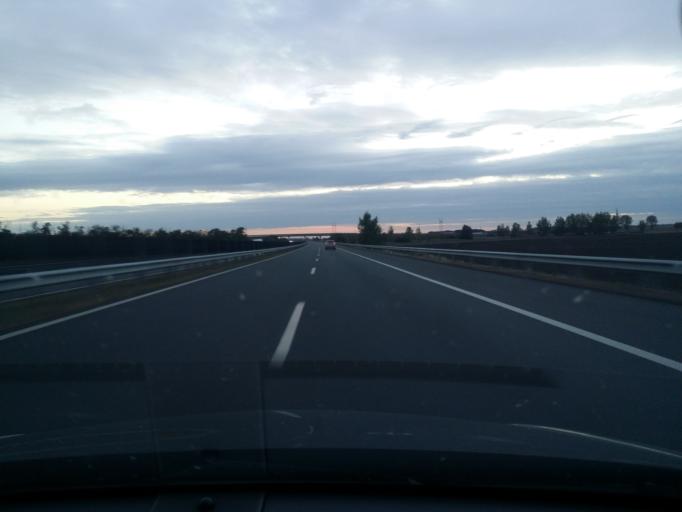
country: HU
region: Hajdu-Bihar
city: Hajdunanas
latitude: 47.8656
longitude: 21.3687
